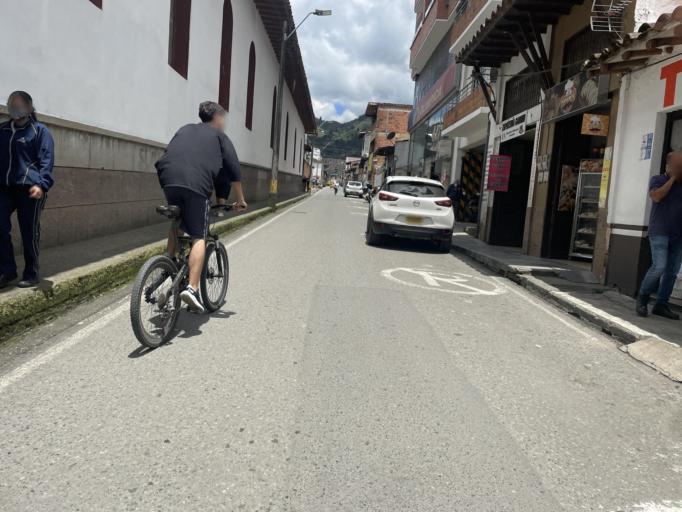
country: CO
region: Antioquia
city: La Ceja
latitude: 6.0313
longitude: -75.4322
